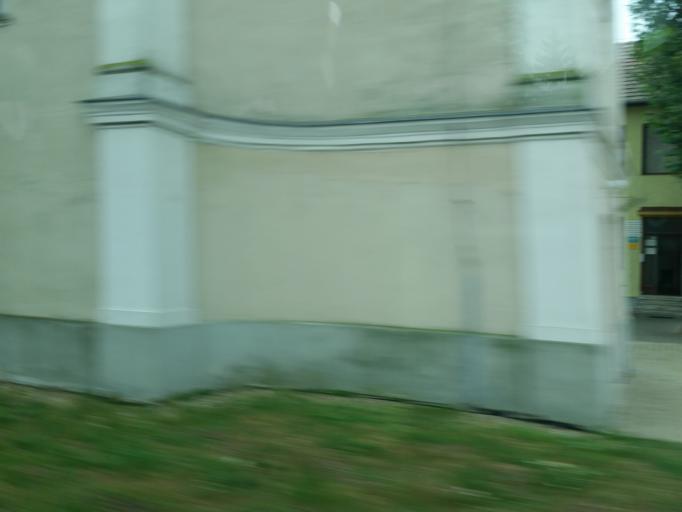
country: HU
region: Gyor-Moson-Sopron
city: Beled
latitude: 47.4763
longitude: 17.1713
